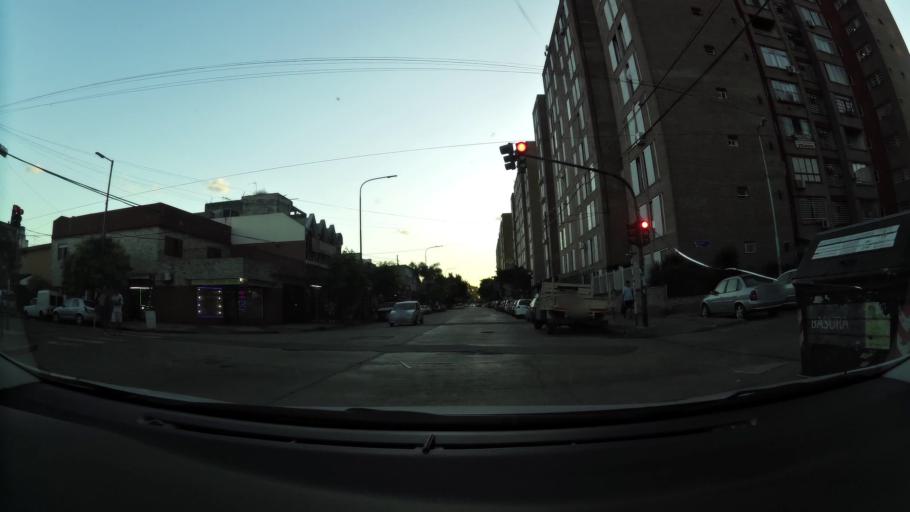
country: AR
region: Buenos Aires F.D.
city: Villa Lugano
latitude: -34.6658
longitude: -58.4717
